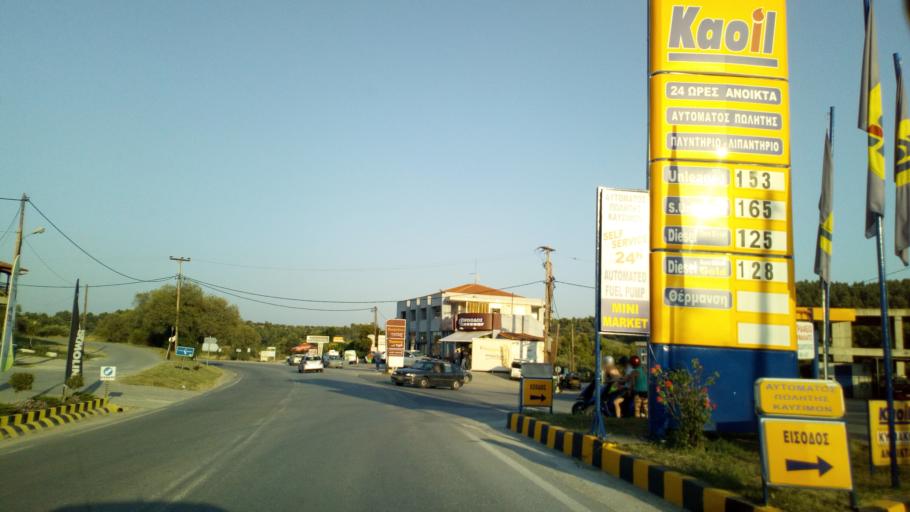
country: GR
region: Central Macedonia
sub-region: Nomos Chalkidikis
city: Pefkochori
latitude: 39.9424
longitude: 23.6681
